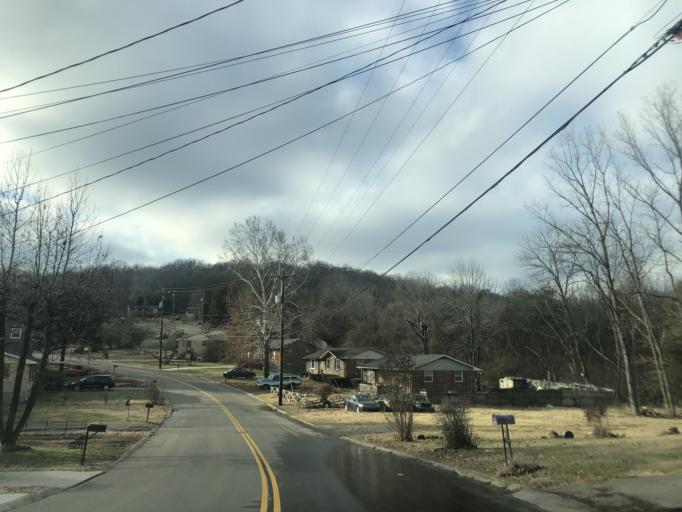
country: US
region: Tennessee
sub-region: Davidson County
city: Nashville
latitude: 36.2195
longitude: -86.7922
